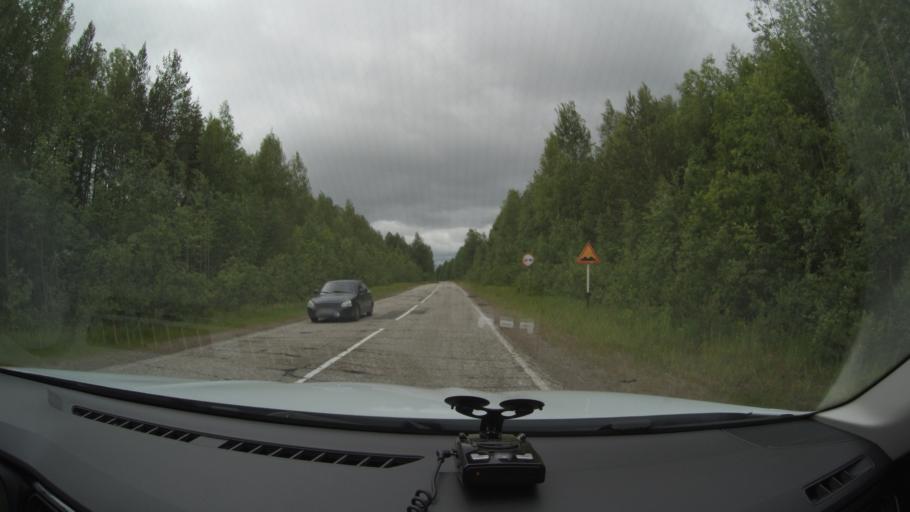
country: RU
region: Komi Republic
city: Nizhniy Odes
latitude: 63.6051
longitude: 54.5096
